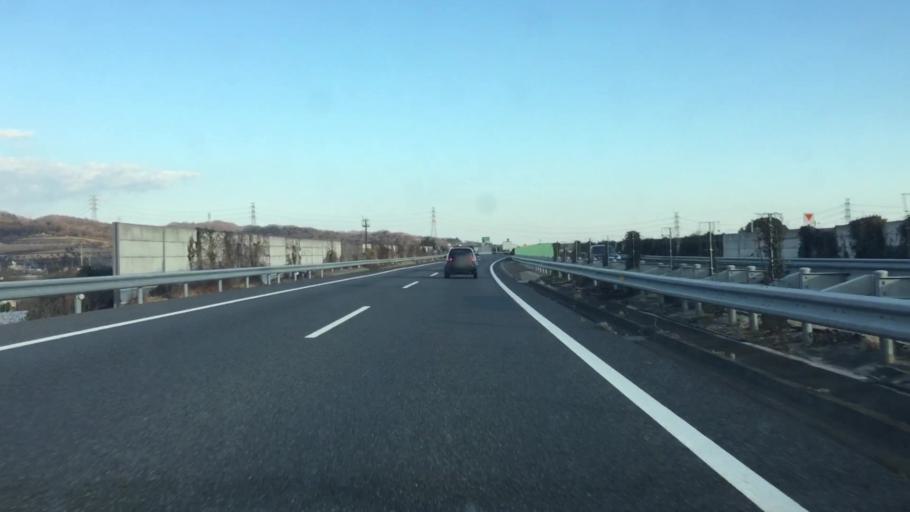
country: JP
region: Gunma
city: Kiryu
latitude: 36.3472
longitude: 139.3216
